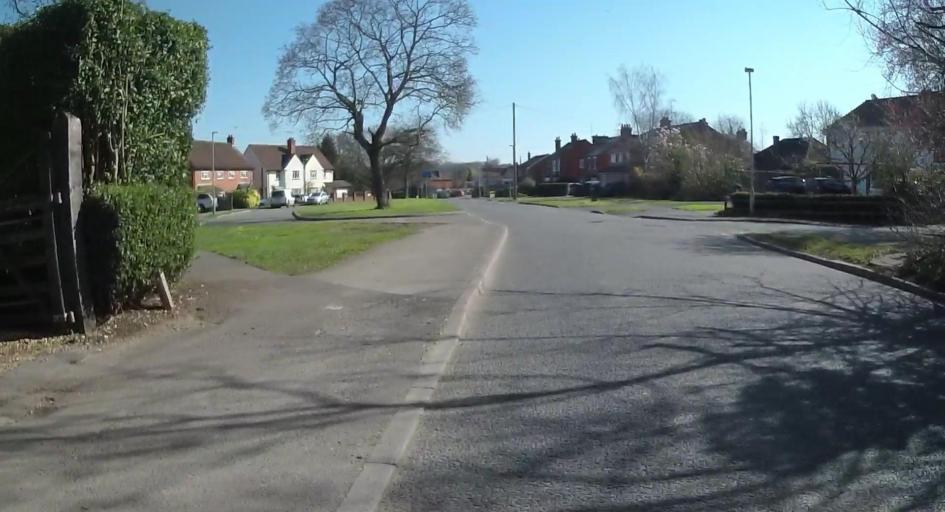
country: GB
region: England
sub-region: Wokingham
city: Wokingham
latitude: 51.4238
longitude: -0.8558
